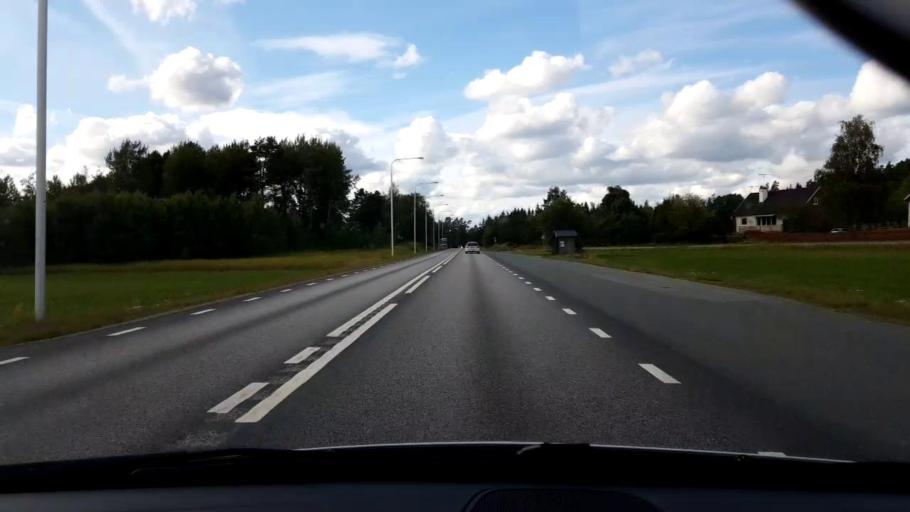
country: SE
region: Joenkoeping
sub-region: Savsjo Kommun
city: Vrigstad
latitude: 57.3611
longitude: 14.4570
